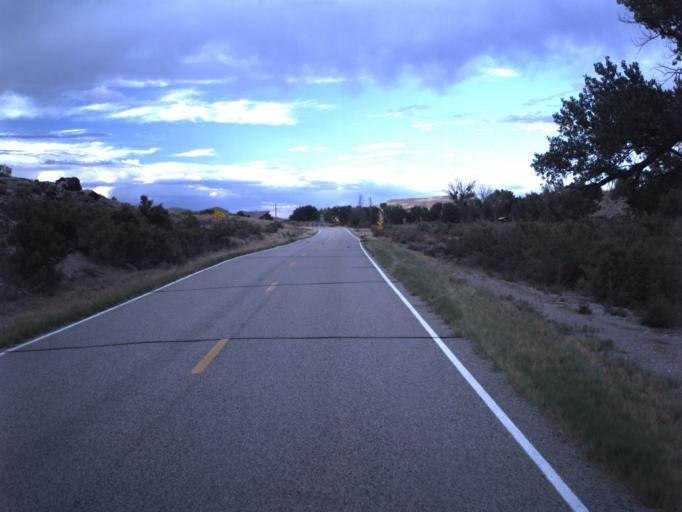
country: US
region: Utah
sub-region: Grand County
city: Moab
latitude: 38.8424
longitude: -109.2838
